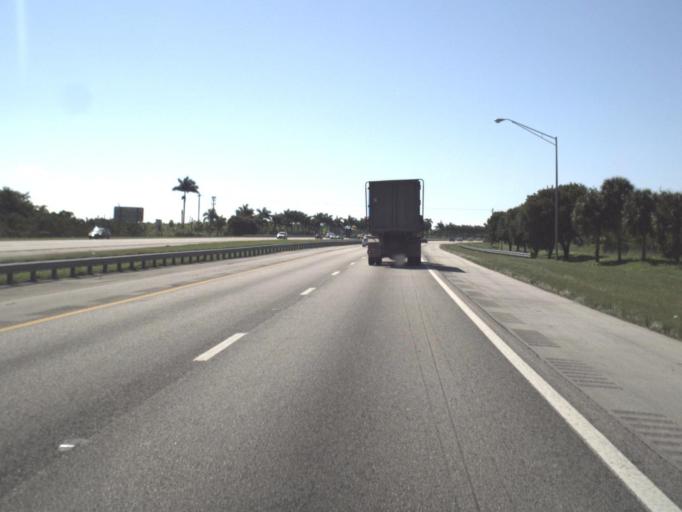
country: US
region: Florida
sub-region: Miami-Dade County
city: Goulds
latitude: 25.5469
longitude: -80.3629
